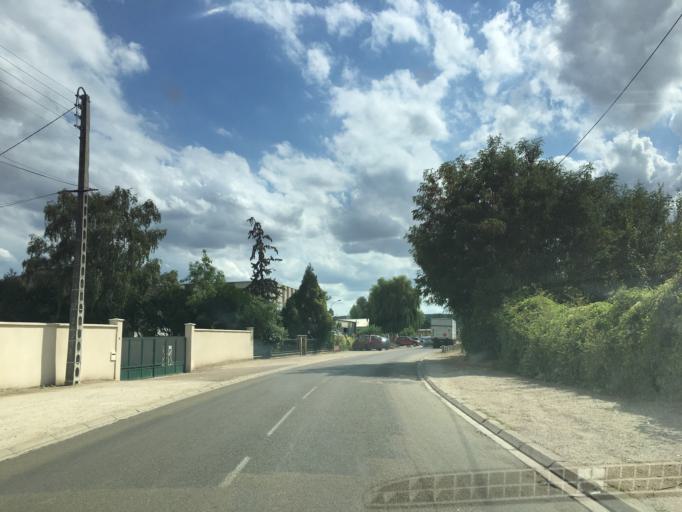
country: FR
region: Bourgogne
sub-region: Departement de l'Yonne
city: Joigny
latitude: 47.9761
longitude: 3.3861
